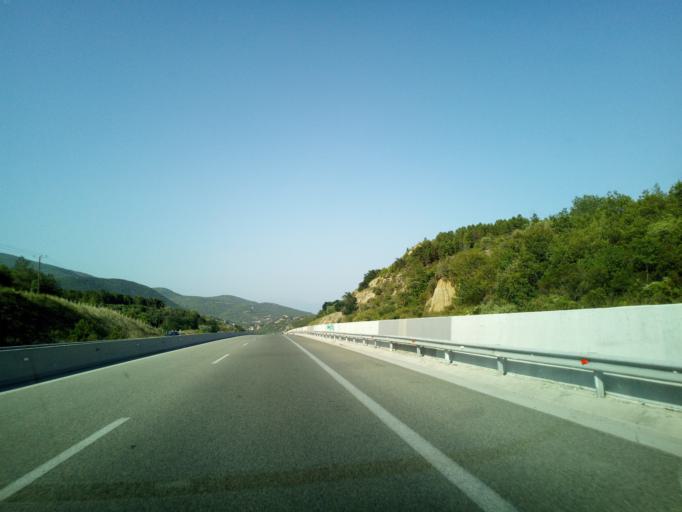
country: GR
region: Central Macedonia
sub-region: Nomos Thessalonikis
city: Nea Vrasna
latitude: 40.6939
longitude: 23.6326
